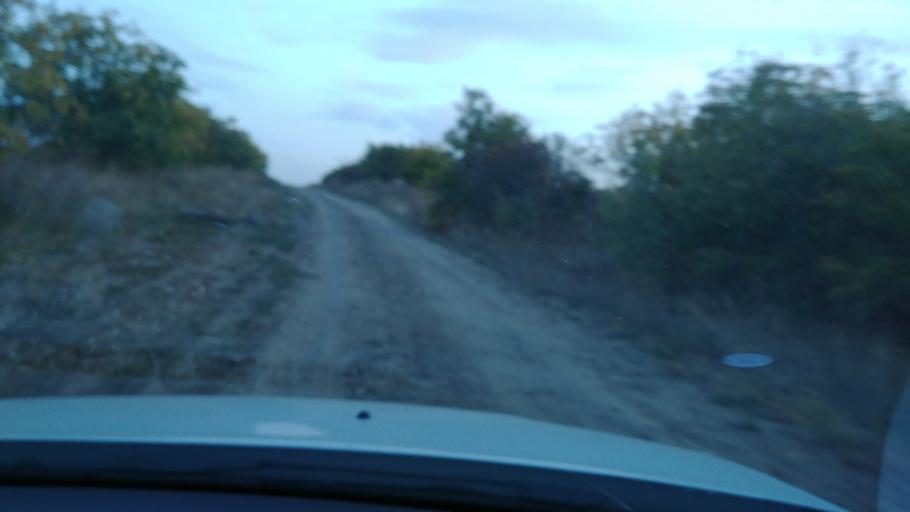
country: MD
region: Rezina
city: Saharna
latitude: 47.6837
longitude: 28.9078
